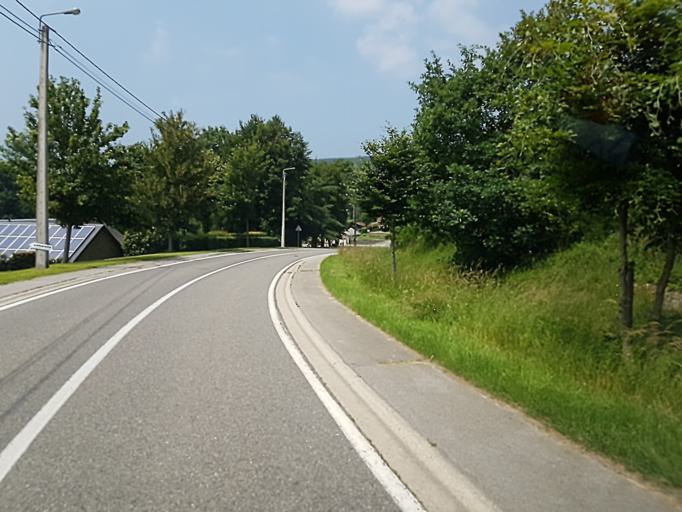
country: BE
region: Wallonia
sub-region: Province de Liege
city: Lierneux
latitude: 50.3285
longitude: 5.7634
